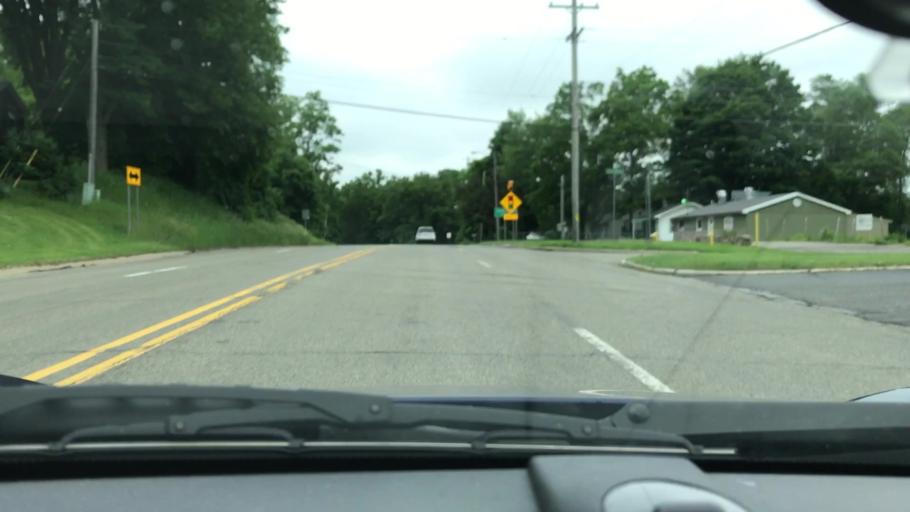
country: US
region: Michigan
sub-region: Calhoun County
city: Springfield
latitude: 42.3580
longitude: -85.2325
